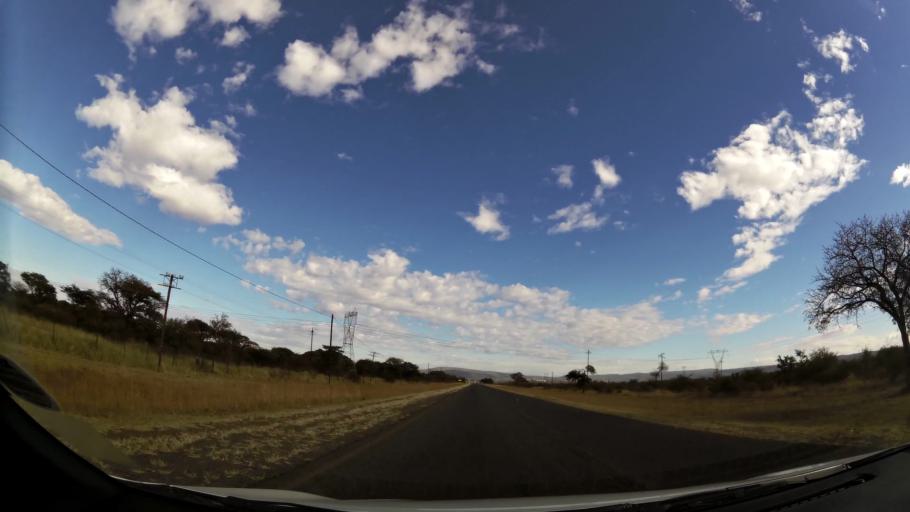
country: ZA
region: Limpopo
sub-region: Waterberg District Municipality
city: Bela-Bela
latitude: -24.9004
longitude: 28.3286
